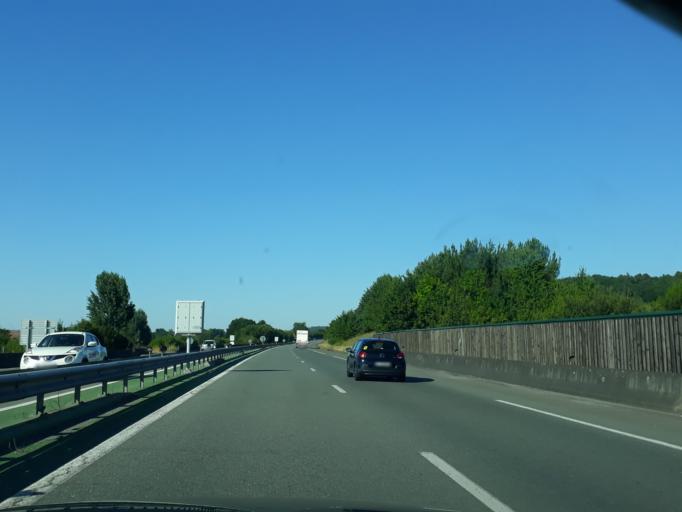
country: FR
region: Aquitaine
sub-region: Departement de la Dordogne
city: Sourzac
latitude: 45.0674
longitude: 0.4331
